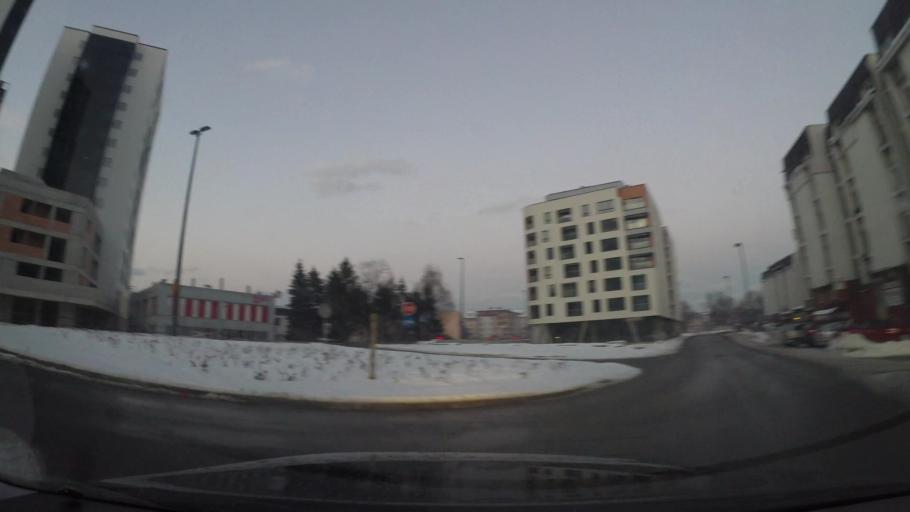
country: BA
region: Federation of Bosnia and Herzegovina
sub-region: Kanton Sarajevo
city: Sarajevo
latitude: 43.8301
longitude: 18.2995
